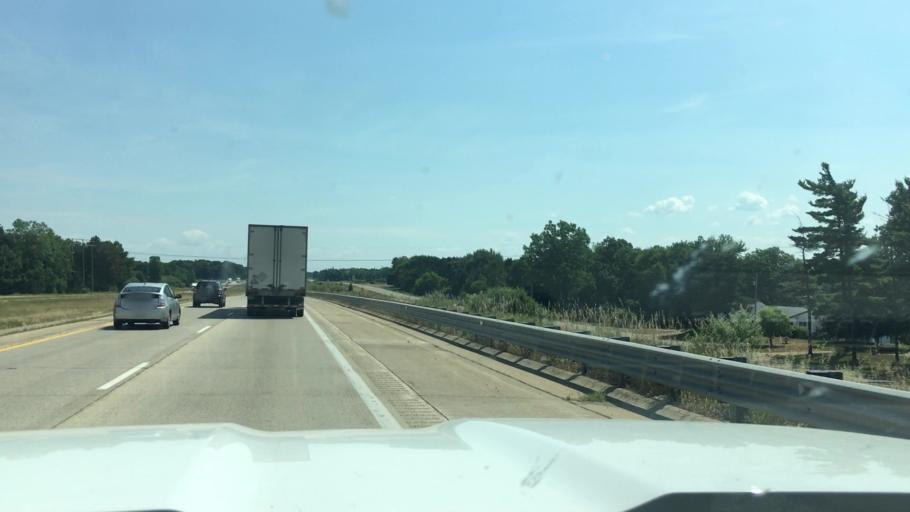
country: US
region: Michigan
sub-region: Shiawassee County
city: Laingsburg
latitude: 42.8064
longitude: -84.3210
